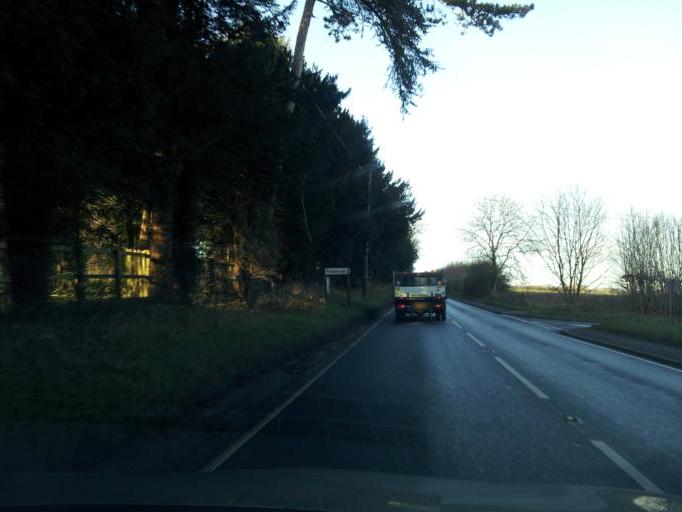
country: GB
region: England
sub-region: Suffolk
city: Bury St Edmunds
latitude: 52.2206
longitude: 0.7395
